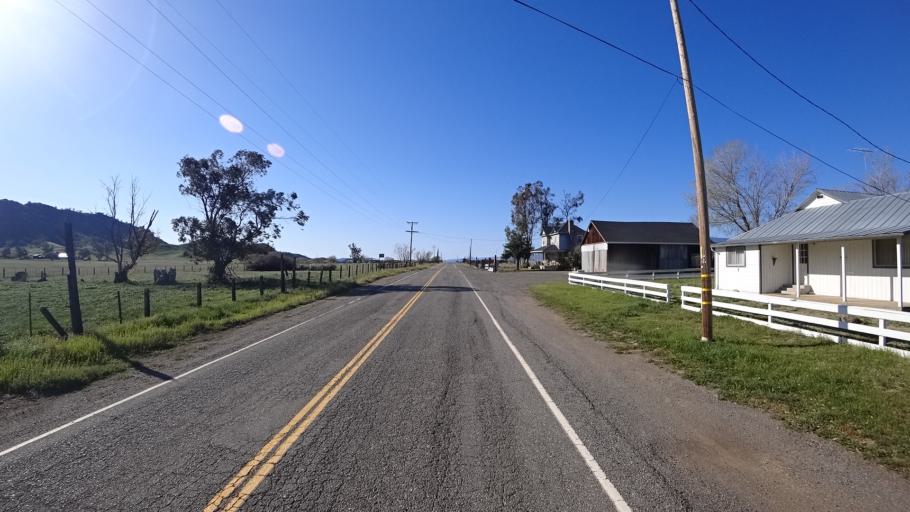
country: US
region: California
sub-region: Tehama County
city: Rancho Tehama Reserve
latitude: 39.7306
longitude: -122.5495
